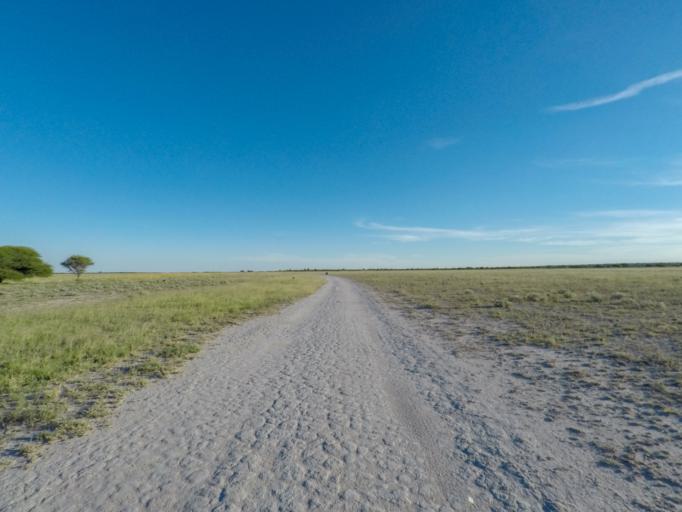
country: BW
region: Central
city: Rakops
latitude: -21.3929
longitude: 23.7938
